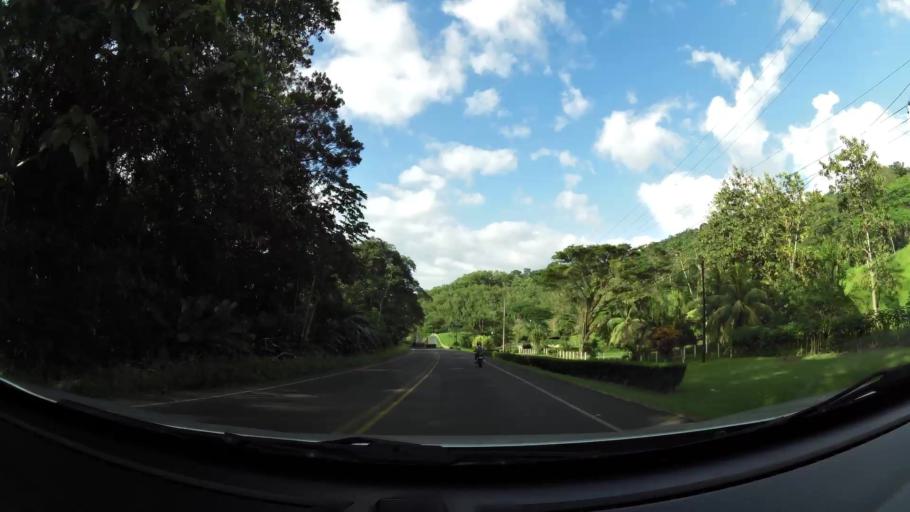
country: CR
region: Puntarenas
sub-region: Canton de Garabito
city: Jaco
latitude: 9.7287
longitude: -84.6262
